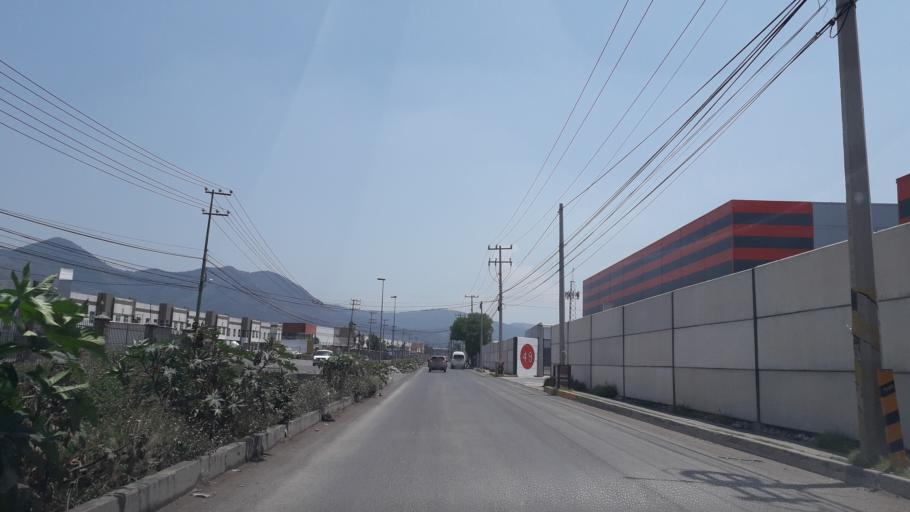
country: MX
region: Mexico
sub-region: Tultitlan
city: Colonia Lazaro Cardenas (Los Hornos)
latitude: 19.6342
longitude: -99.1532
